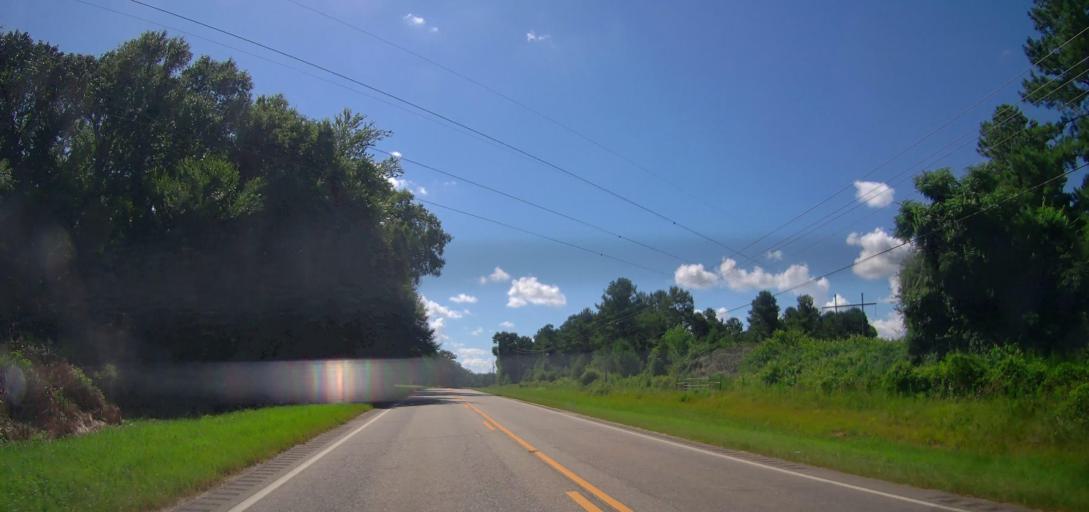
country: US
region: Alabama
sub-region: Elmore County
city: Tallassee
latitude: 32.3794
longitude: -85.8676
